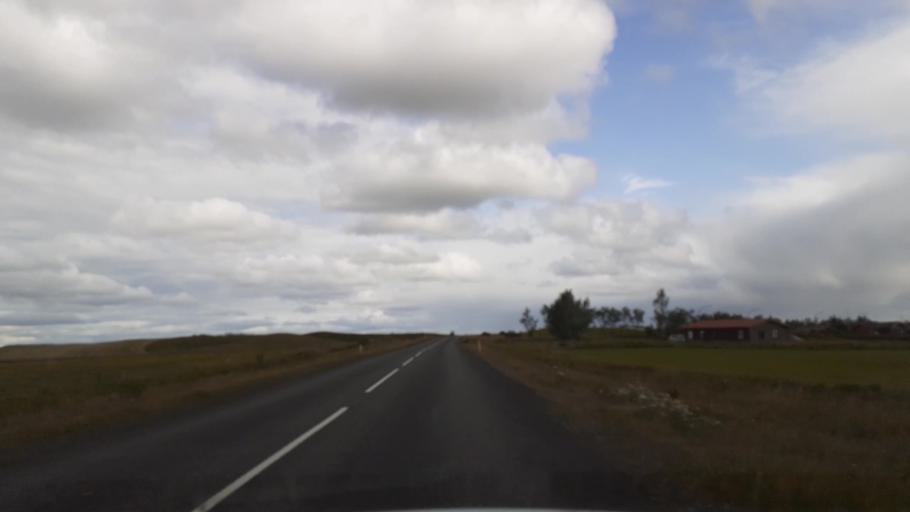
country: IS
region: South
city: Vestmannaeyjar
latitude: 63.8318
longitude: -20.4224
